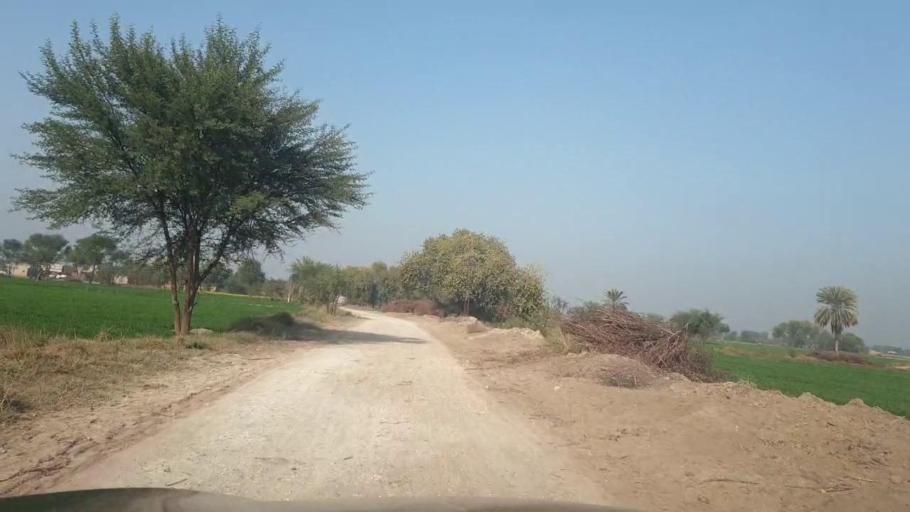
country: PK
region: Sindh
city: Ubauro
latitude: 28.0931
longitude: 69.8412
